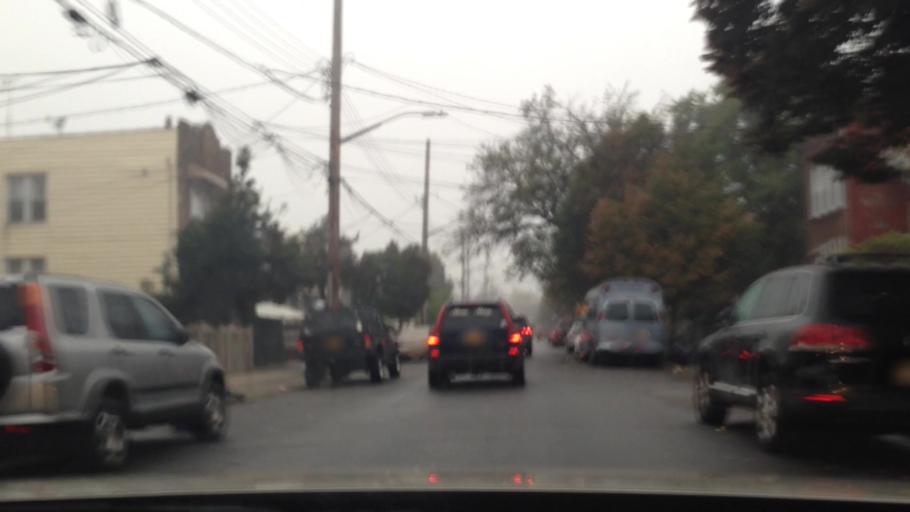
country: US
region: New York
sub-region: Kings County
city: East New York
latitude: 40.6618
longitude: -73.8844
